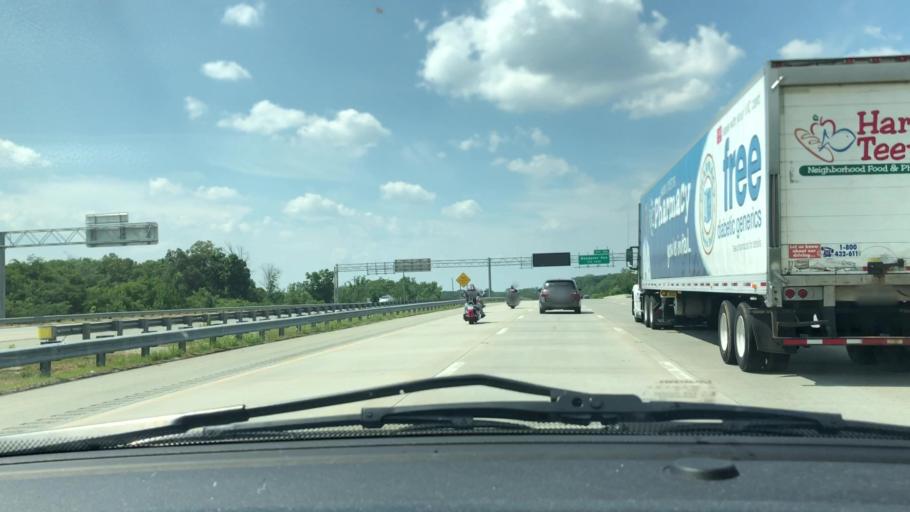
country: US
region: North Carolina
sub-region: Guilford County
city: Jamestown
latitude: 36.0342
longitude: -79.8889
